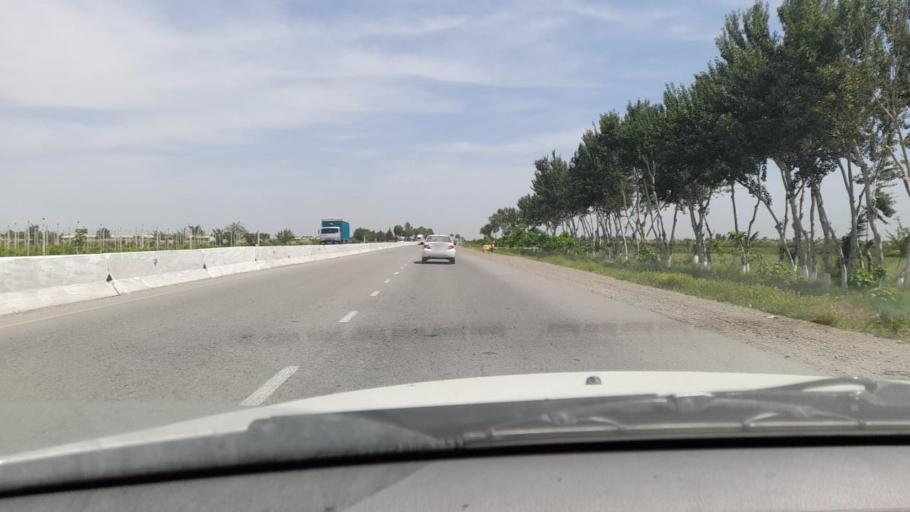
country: UZ
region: Bukhara
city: Galaosiyo
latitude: 39.8911
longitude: 64.4667
